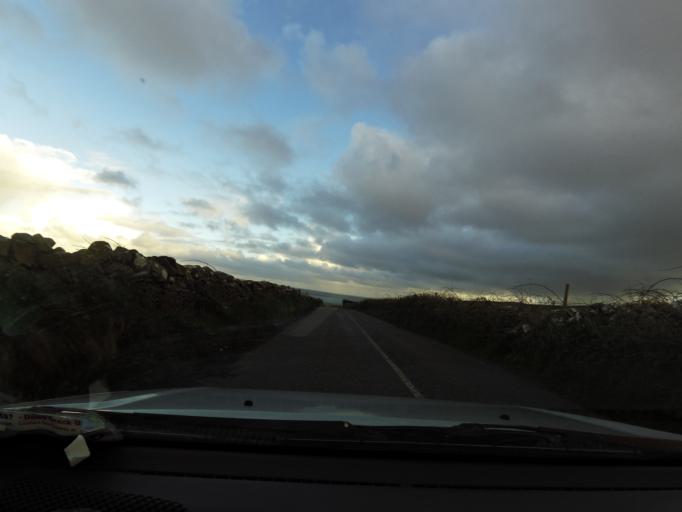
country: IE
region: Munster
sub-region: An Clar
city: Kilrush
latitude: 52.9590
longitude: -9.4223
